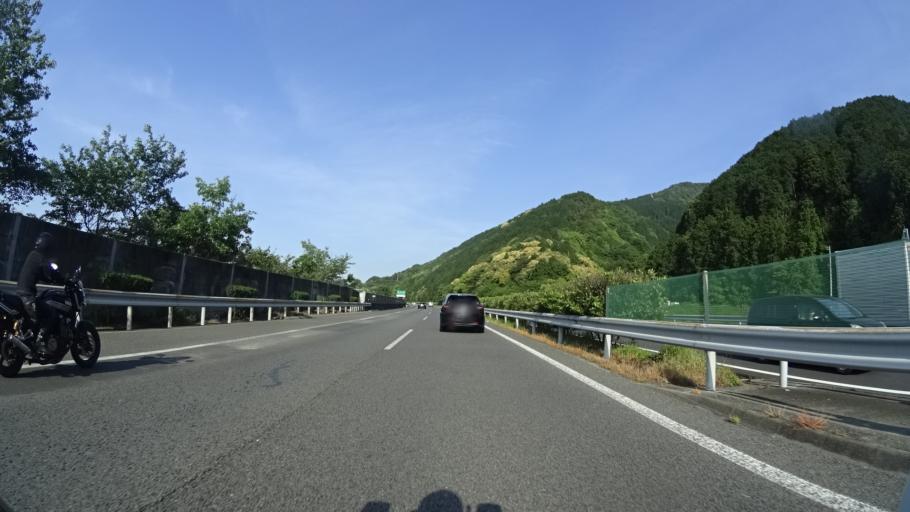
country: JP
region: Ehime
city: Niihama
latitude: 33.9292
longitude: 133.3413
